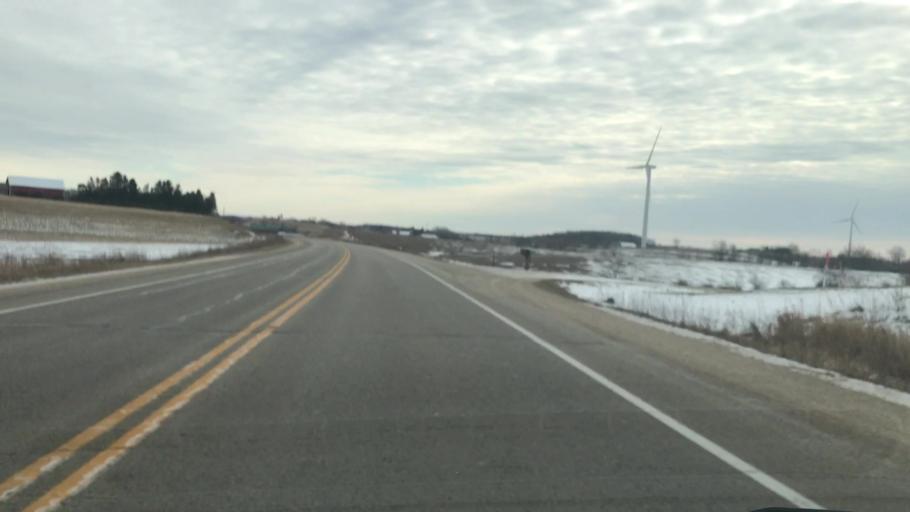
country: US
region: Wisconsin
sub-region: Dodge County
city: Theresa
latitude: 43.4368
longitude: -88.4745
